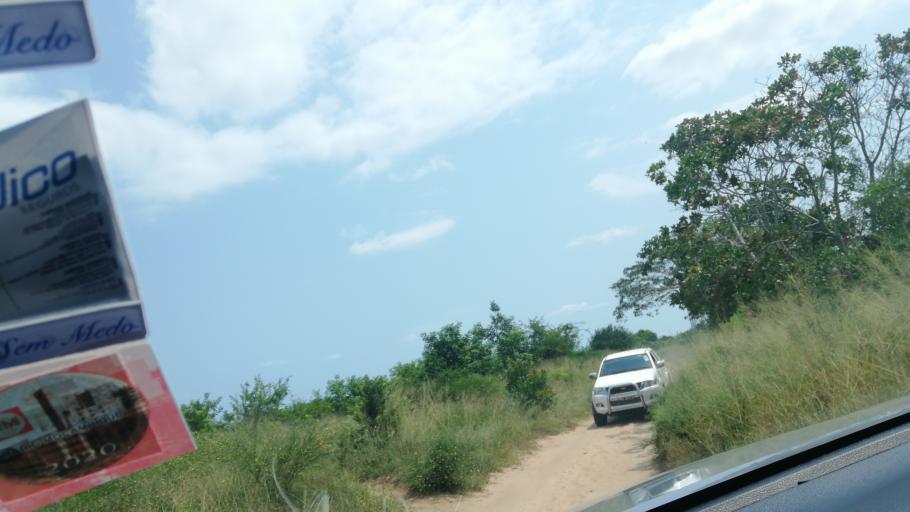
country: MZ
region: Maputo
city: Matola
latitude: -26.1106
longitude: 32.4273
